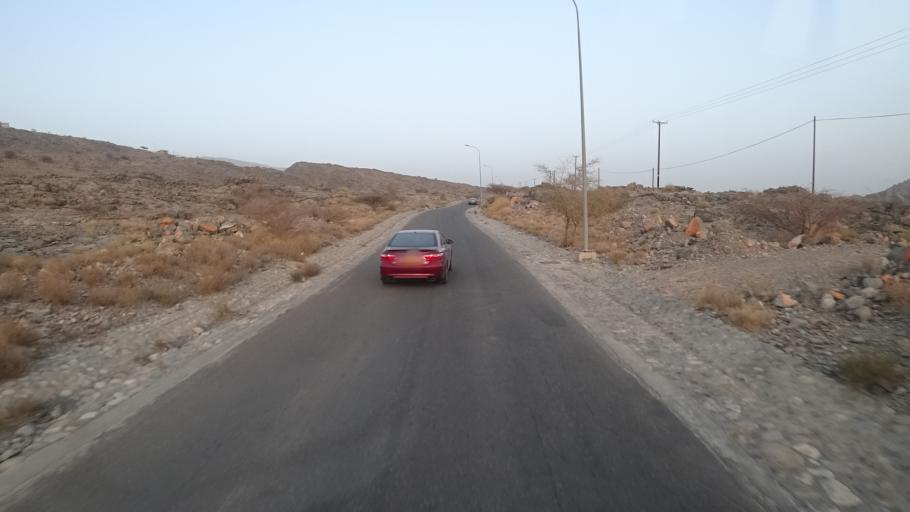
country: OM
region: Muhafazat ad Dakhiliyah
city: Bahla'
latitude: 23.1292
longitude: 57.3012
